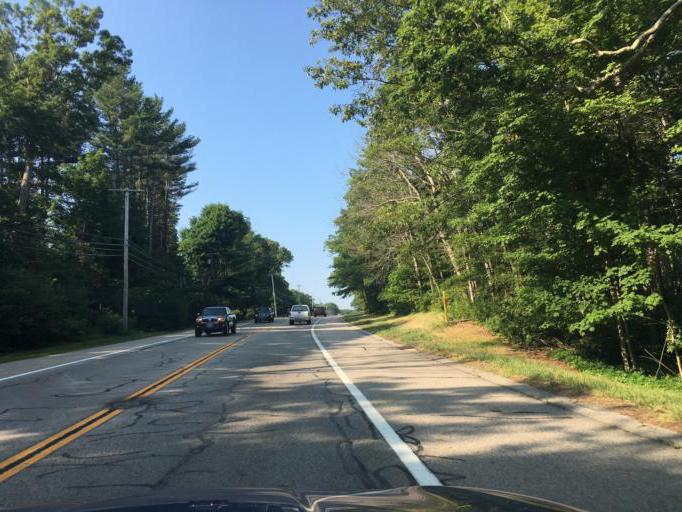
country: US
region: Rhode Island
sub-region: Washington County
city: Exeter
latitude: 41.5428
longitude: -71.5360
